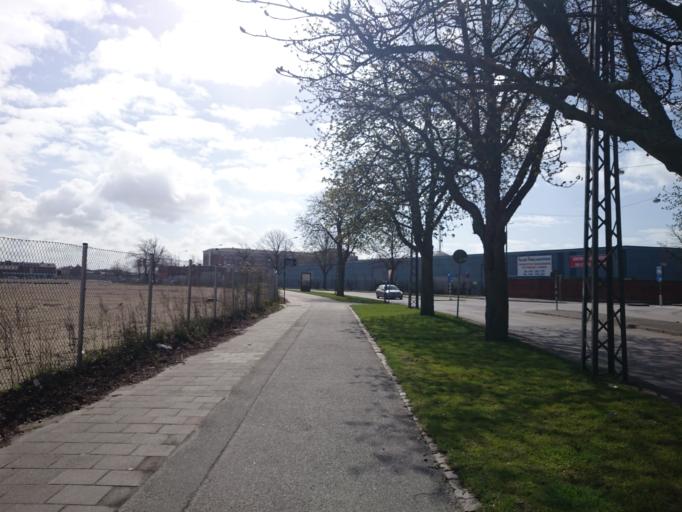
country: SE
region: Skane
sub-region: Malmo
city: Malmoe
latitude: 55.6011
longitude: 13.0203
